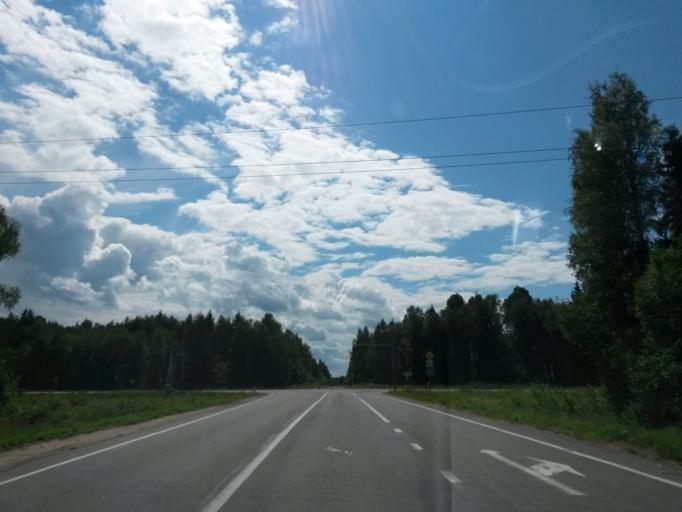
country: RU
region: Jaroslavl
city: Gavrilov-Yam
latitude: 57.2733
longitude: 39.9502
